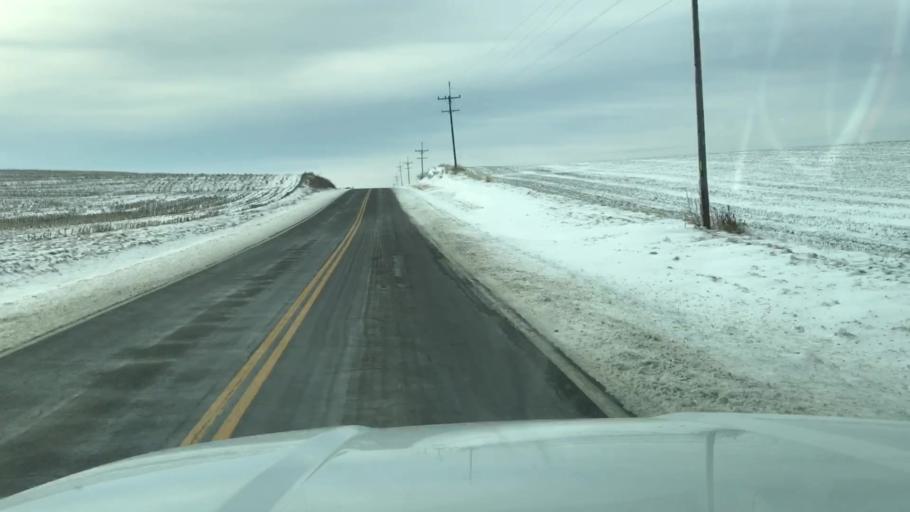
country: US
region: Missouri
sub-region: Holt County
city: Mound City
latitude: 40.1072
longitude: -95.1449
